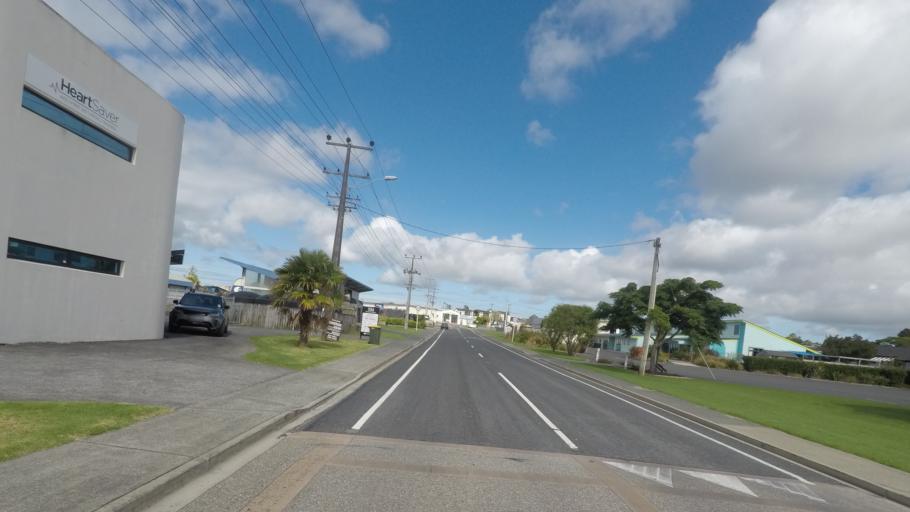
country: NZ
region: Auckland
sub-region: Auckland
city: Muriwai Beach
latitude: -36.7715
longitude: 174.5457
